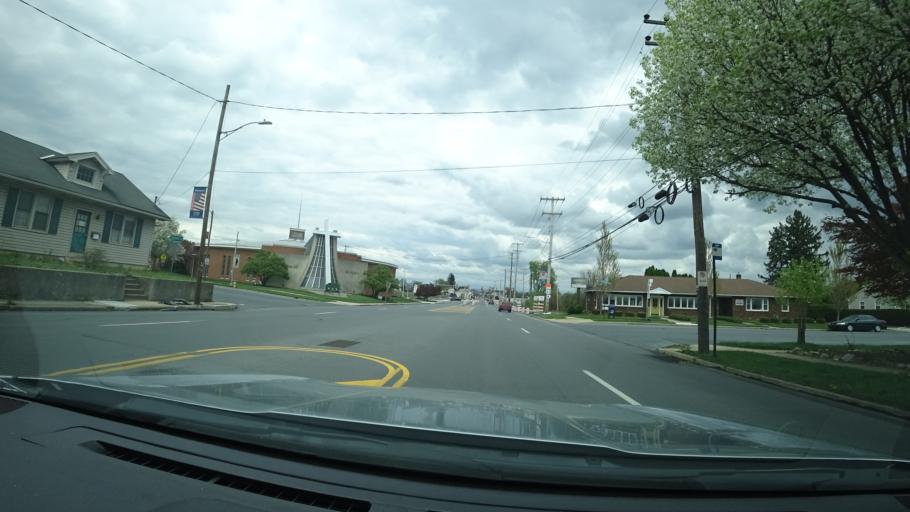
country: US
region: Pennsylvania
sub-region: Lehigh County
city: Fullerton
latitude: 40.6290
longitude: -75.4699
